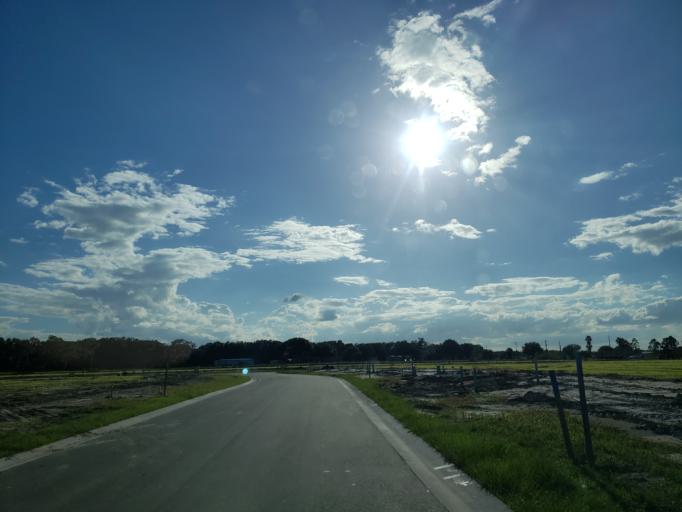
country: US
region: Florida
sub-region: Hillsborough County
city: Boyette
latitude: 27.8102
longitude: -82.2326
